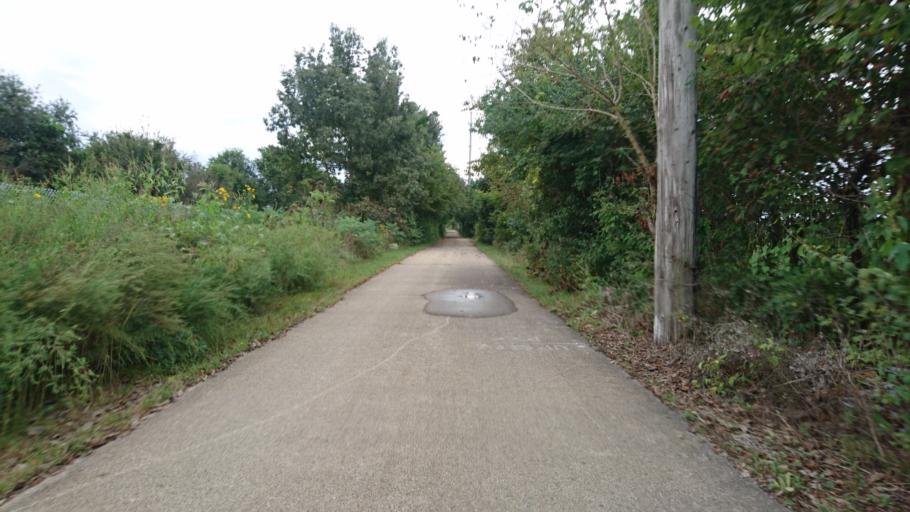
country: US
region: Illinois
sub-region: Sangamon County
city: Chatham
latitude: 39.6949
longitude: -89.6937
